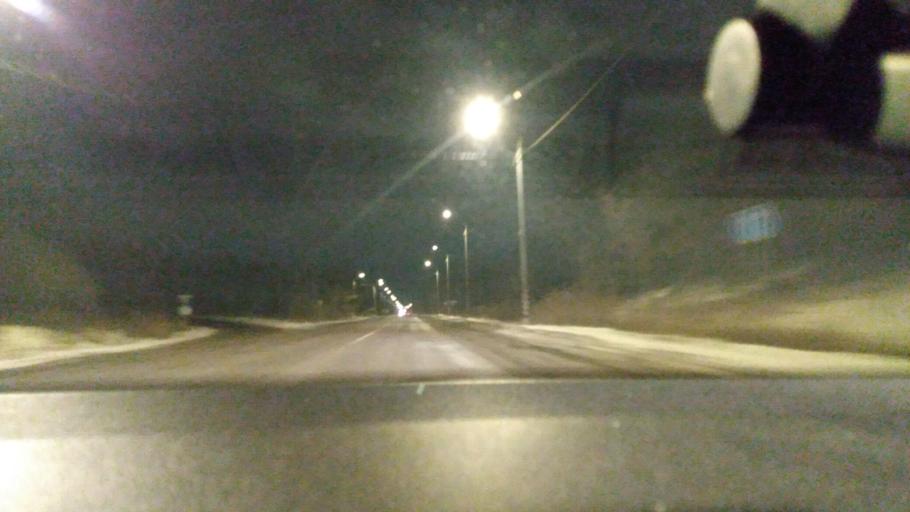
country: RU
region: Moskovskaya
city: Yegor'yevsk
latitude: 55.4155
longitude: 39.0455
